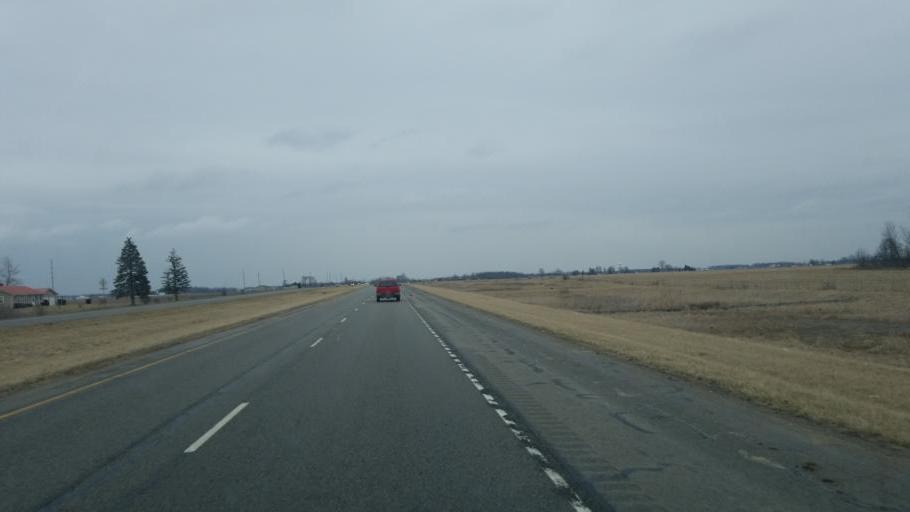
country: US
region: Indiana
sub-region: Adams County
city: Decatur
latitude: 40.7721
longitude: -84.9376
